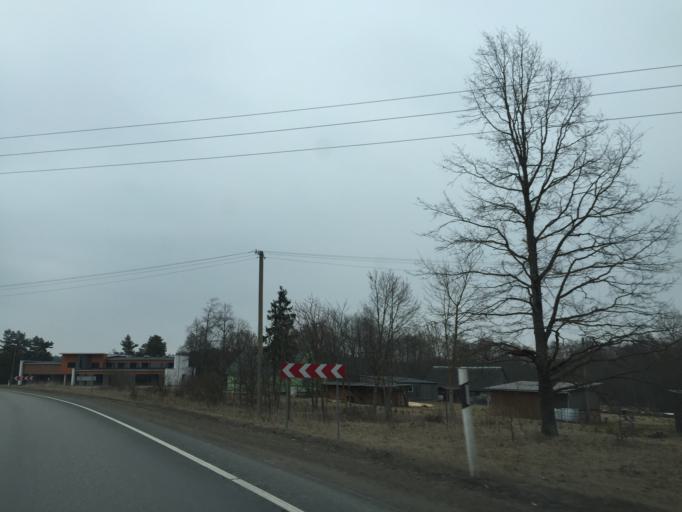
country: EE
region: Paernumaa
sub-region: Paikuse vald
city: Paikuse
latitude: 58.2948
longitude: 24.6058
